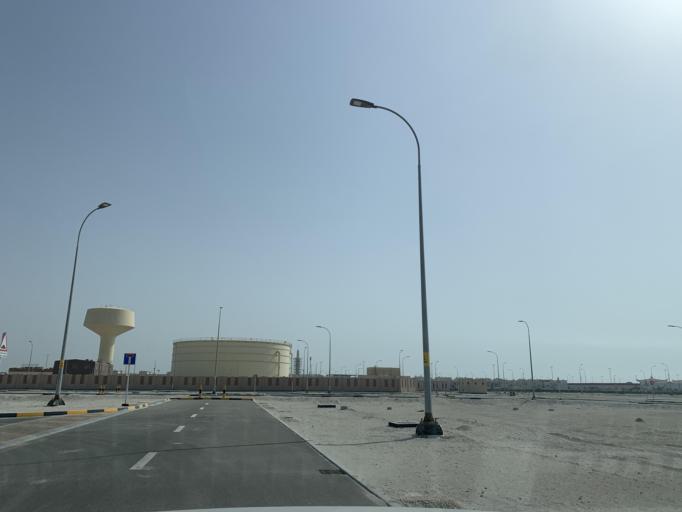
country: BH
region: Muharraq
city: Al Muharraq
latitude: 26.3073
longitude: 50.6338
